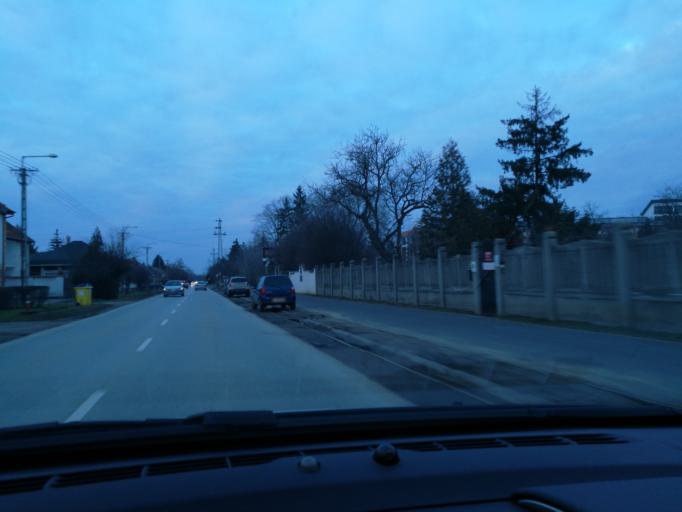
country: HU
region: Szabolcs-Szatmar-Bereg
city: Nyiregyhaza
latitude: 47.9707
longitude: 21.7081
